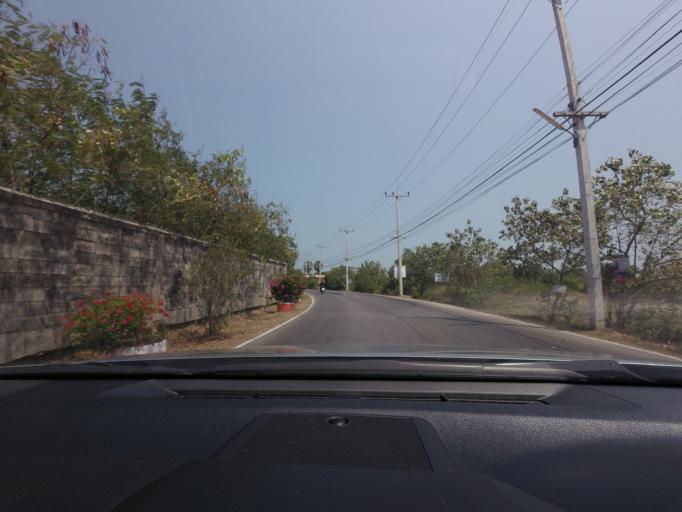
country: TH
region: Phetchaburi
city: Cha-am
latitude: 12.8185
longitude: 99.9849
